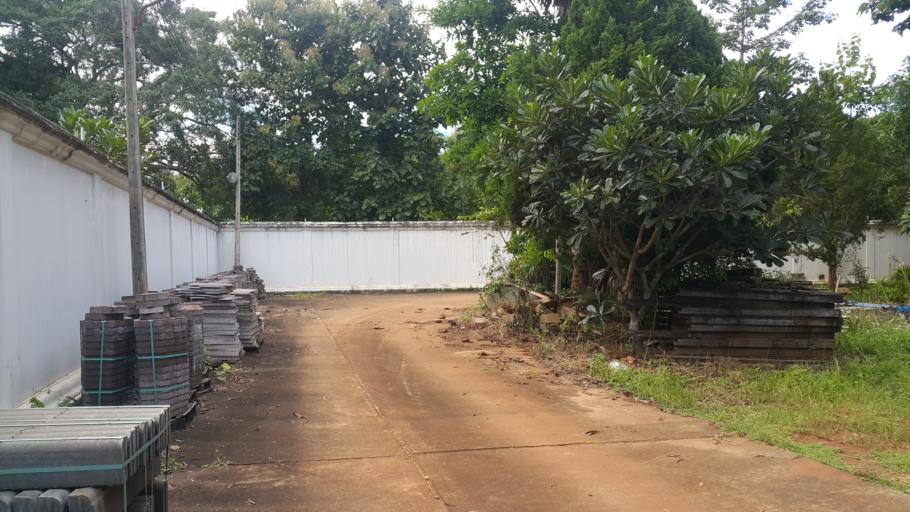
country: TH
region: Chiang Mai
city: Mae Taeng
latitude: 19.1583
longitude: 98.9761
